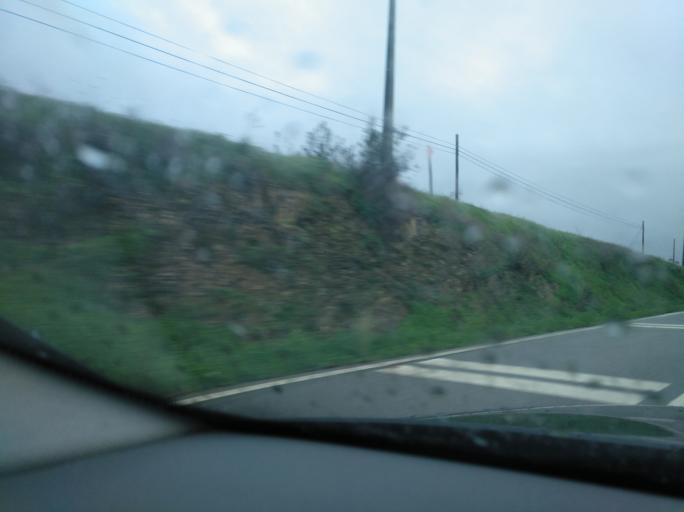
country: PT
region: Beja
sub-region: Mertola
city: Mertola
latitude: 37.5417
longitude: -7.6447
